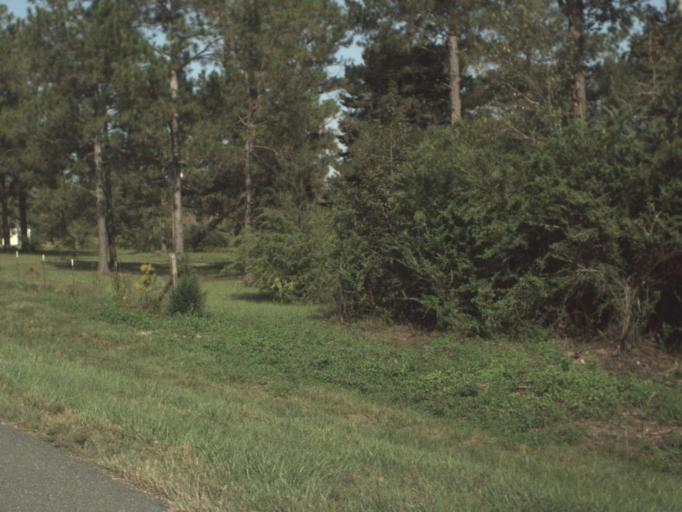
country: US
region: Florida
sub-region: Jackson County
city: Graceville
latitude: 30.9645
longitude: -85.5954
